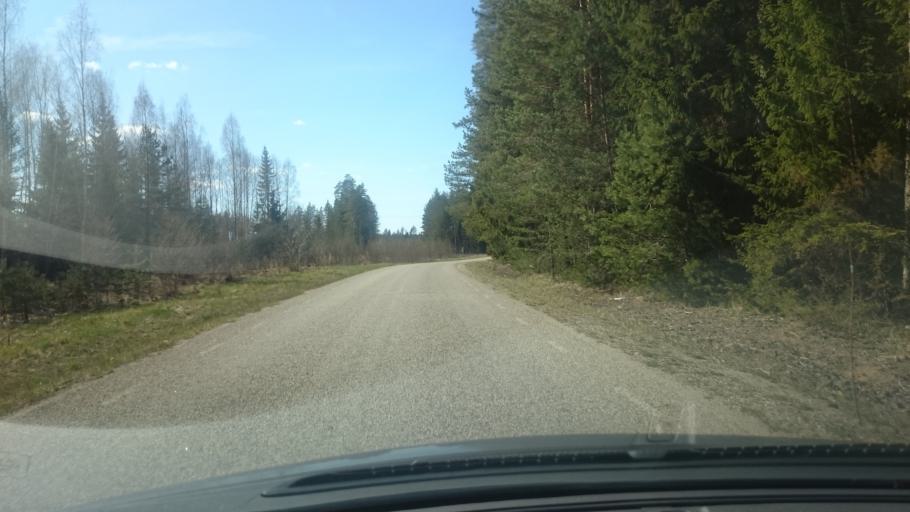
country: EE
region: Polvamaa
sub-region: Polva linn
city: Polva
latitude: 58.1203
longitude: 27.0292
